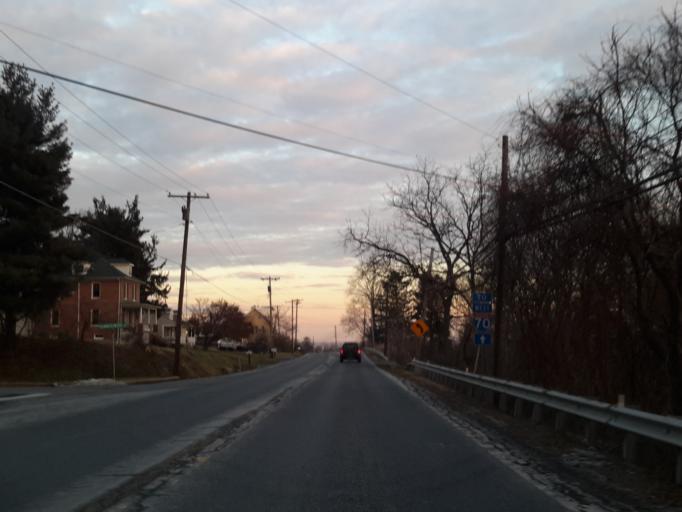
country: US
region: Maryland
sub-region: Frederick County
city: Braddock Heights
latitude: 39.4211
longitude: -77.4818
